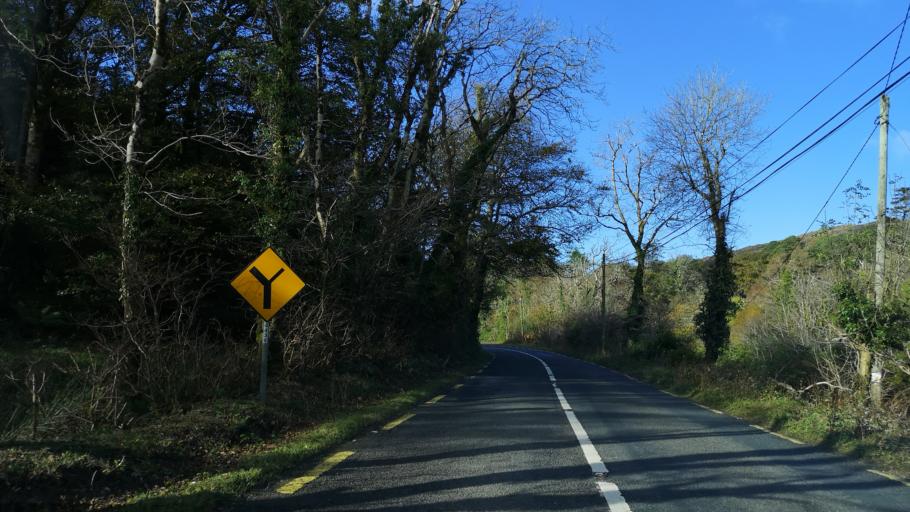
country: IE
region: Connaught
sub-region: County Galway
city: Clifden
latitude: 53.5608
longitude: -9.9152
